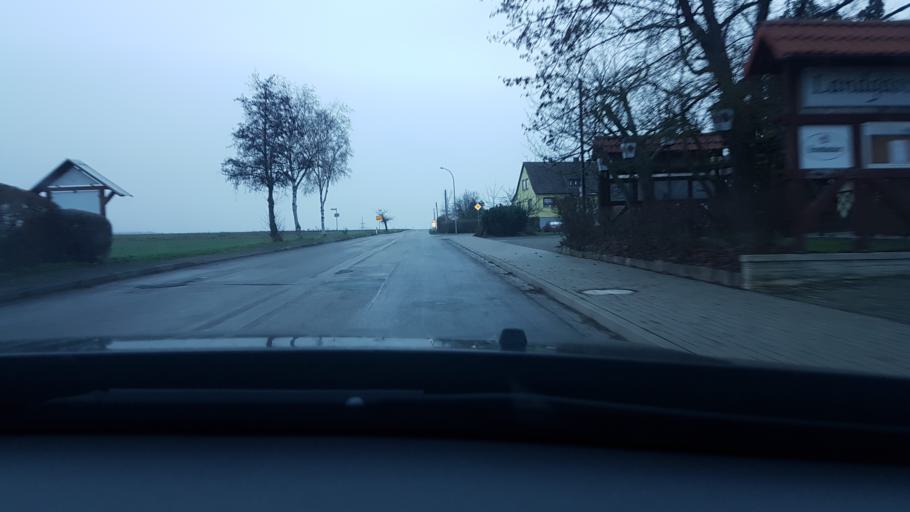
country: DE
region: Hesse
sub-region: Regierungsbezirk Kassel
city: Korbach
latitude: 51.3299
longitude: 8.9091
